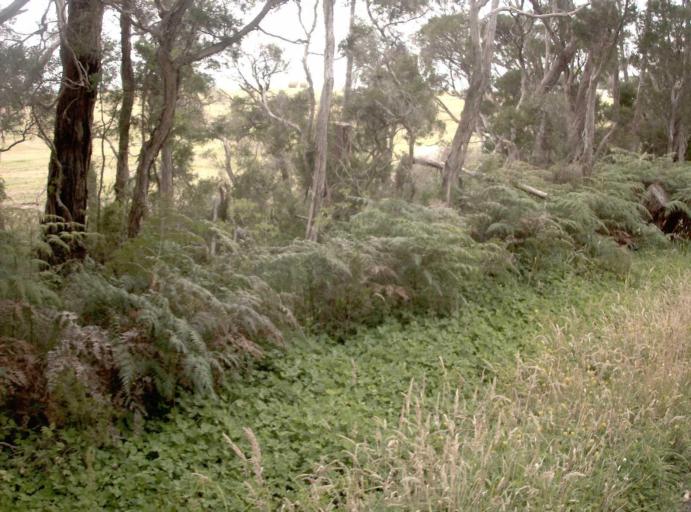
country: AU
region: Victoria
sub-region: Cardinia
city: Koo-Wee-Rup
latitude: -38.3435
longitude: 145.6528
